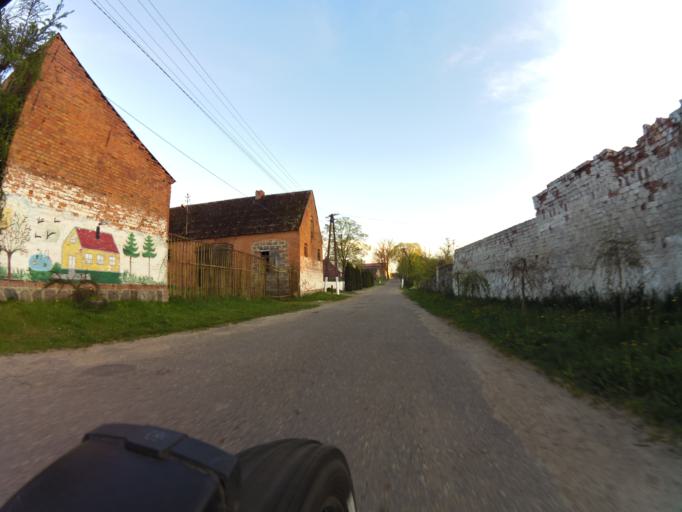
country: PL
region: West Pomeranian Voivodeship
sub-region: Powiat lobeski
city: Lobez
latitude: 53.6986
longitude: 15.6454
